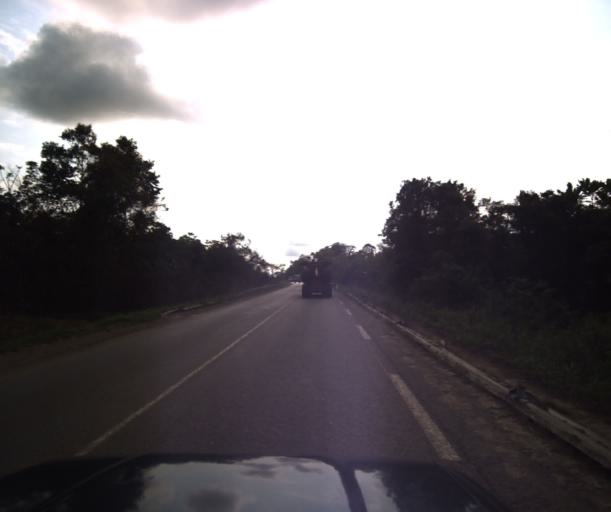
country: CM
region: Littoral
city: Dizangue
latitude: 3.9495
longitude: 10.0196
